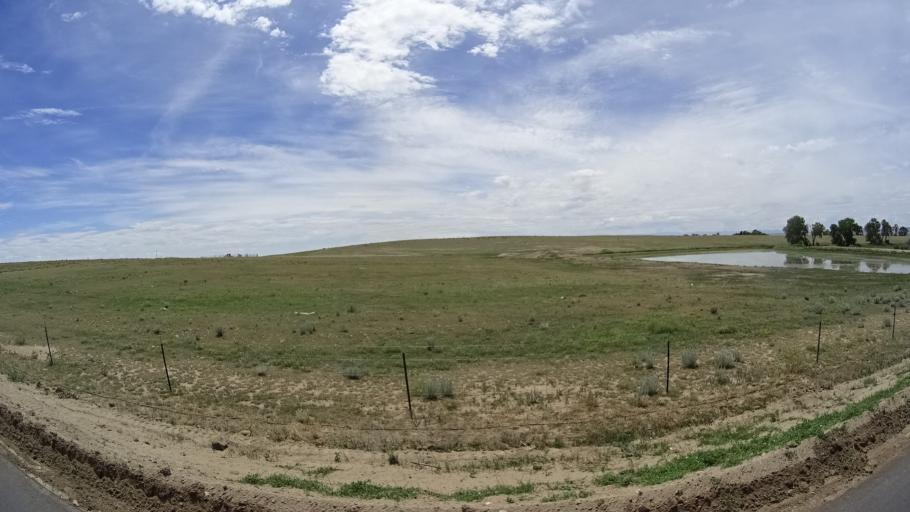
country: US
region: Colorado
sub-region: El Paso County
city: Fountain
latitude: 38.6940
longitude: -104.6526
